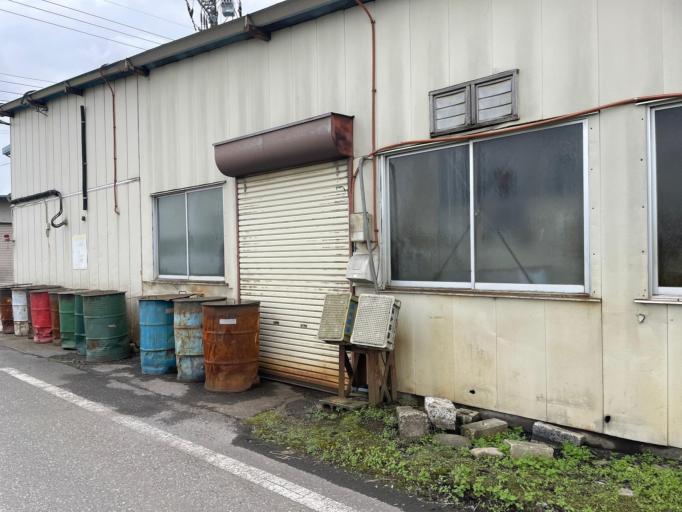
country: JP
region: Tochigi
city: Kanuma
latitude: 36.4862
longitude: 139.7544
